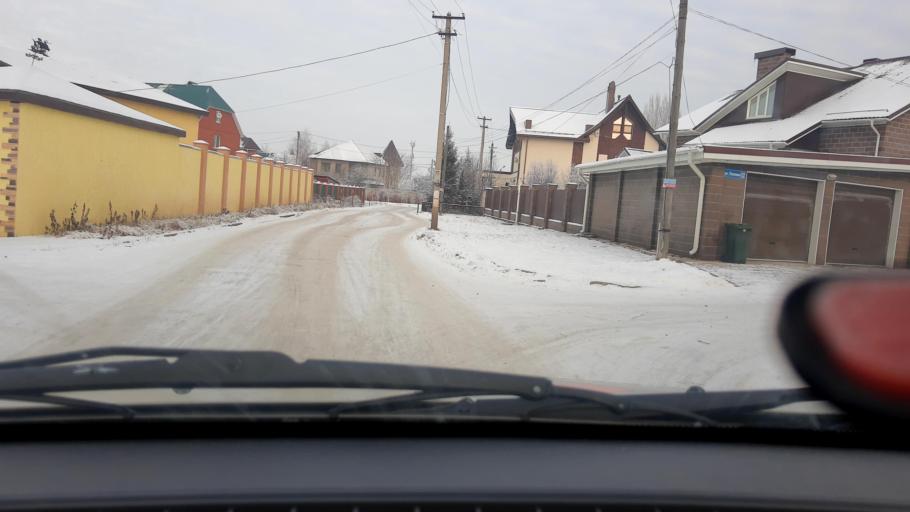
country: RU
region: Bashkortostan
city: Mikhaylovka
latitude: 54.7957
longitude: 55.9446
